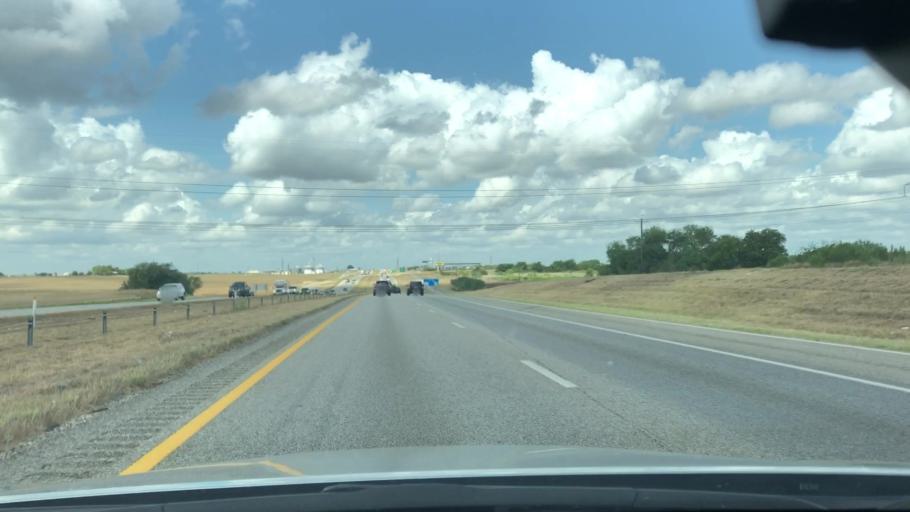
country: US
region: Texas
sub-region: Guadalupe County
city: McQueeney
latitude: 29.5452
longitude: -98.0578
